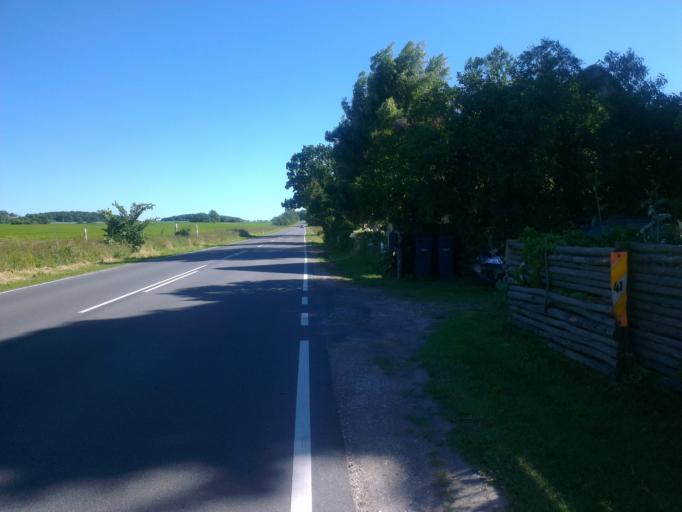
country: DK
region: Capital Region
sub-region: Frederikssund Kommune
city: Jaegerspris
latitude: 55.8863
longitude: 11.9552
